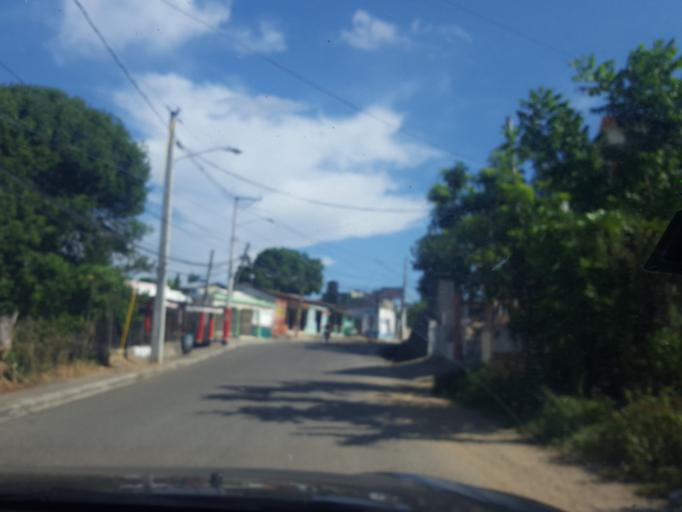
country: DO
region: La Vega
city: Rio Verde Arriba
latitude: 19.3627
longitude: -70.6050
